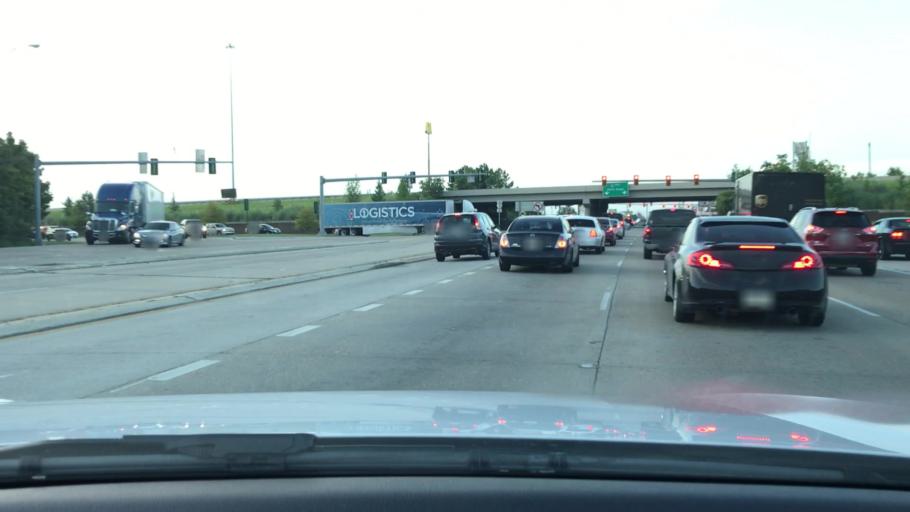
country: US
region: Louisiana
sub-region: East Baton Rouge Parish
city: Village Saint George
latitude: 30.3808
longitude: -91.0667
